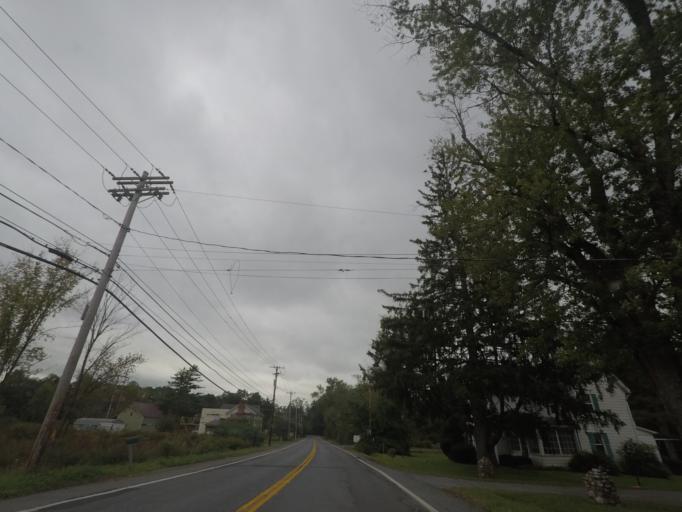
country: US
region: New York
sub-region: Rensselaer County
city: Hoosick Falls
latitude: 42.9147
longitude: -73.3521
